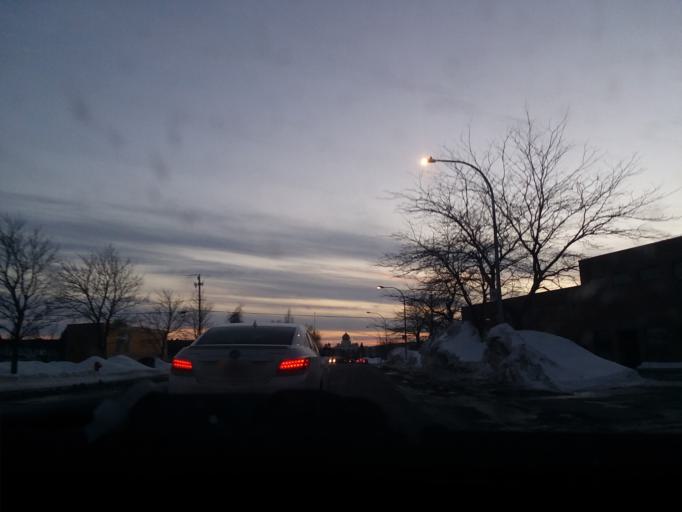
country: CA
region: Quebec
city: Montreal-Ouest
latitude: 45.4437
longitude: -73.6270
